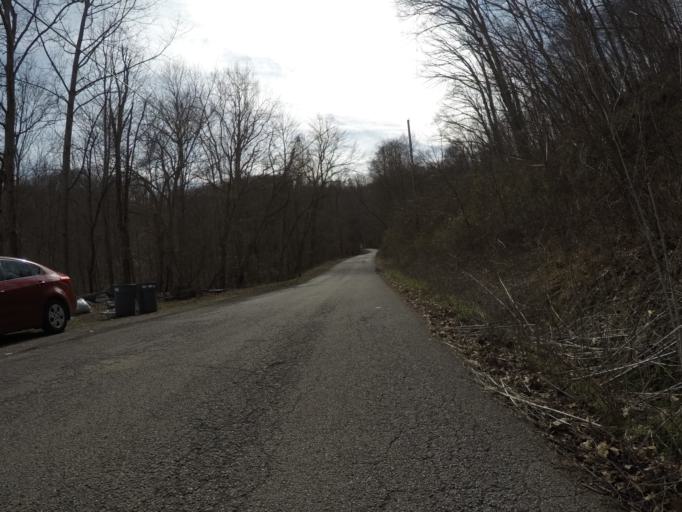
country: US
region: West Virginia
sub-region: Wayne County
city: Lavalette
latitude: 38.3440
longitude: -82.5071
